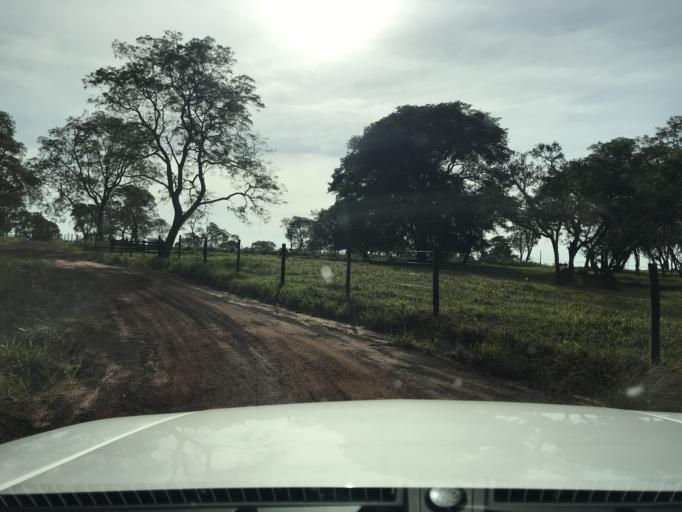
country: BR
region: Mato Grosso do Sul
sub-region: Iguatemi
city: Iguatemi
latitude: -23.6451
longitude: -54.5746
